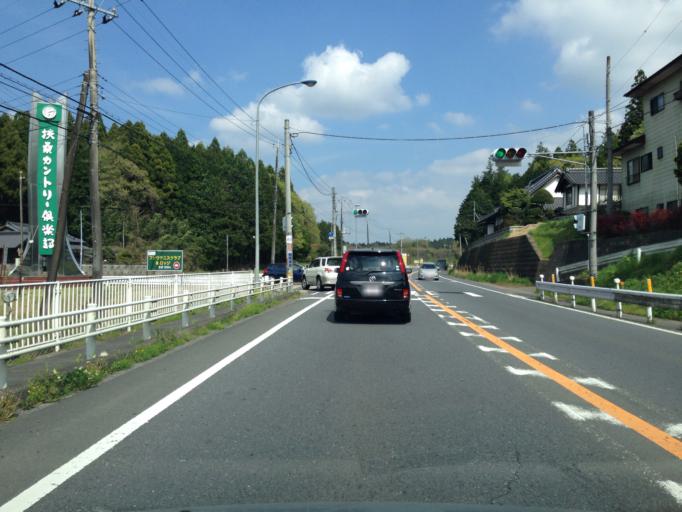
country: JP
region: Ibaraki
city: Tomobe
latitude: 36.3834
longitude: 140.3031
